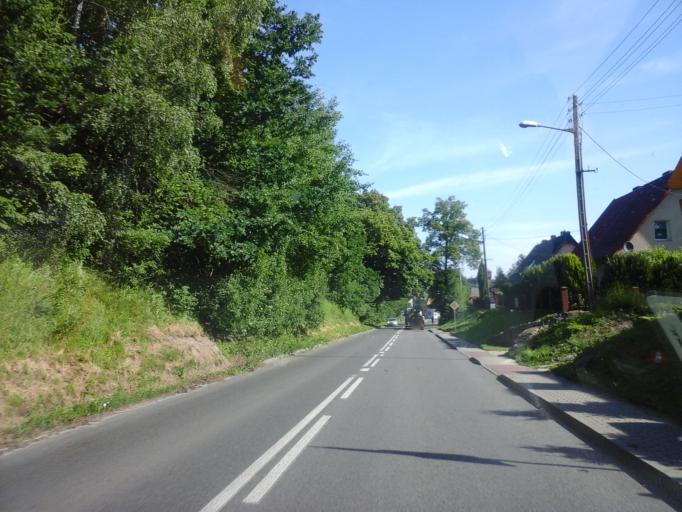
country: PL
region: West Pomeranian Voivodeship
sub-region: Powiat swidwinski
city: Polczyn-Zdroj
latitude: 53.7596
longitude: 16.0960
